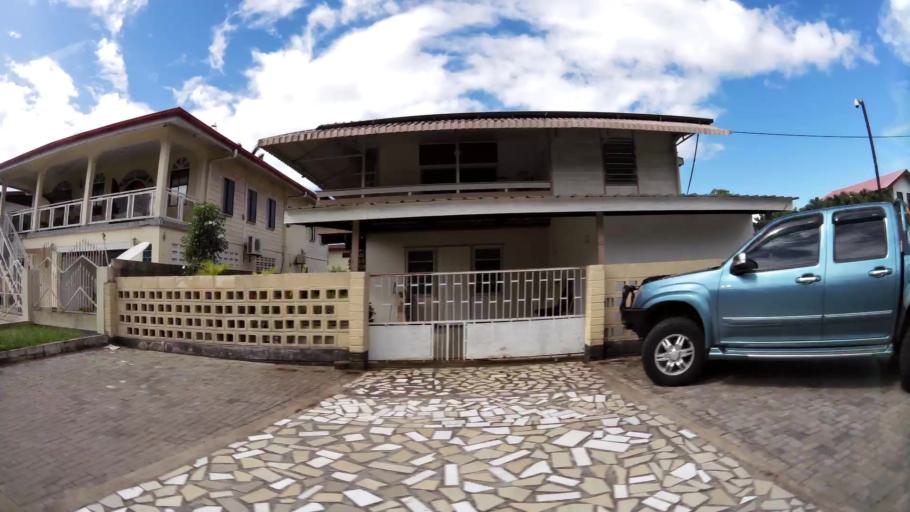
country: SR
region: Paramaribo
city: Paramaribo
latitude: 5.8464
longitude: -55.1491
